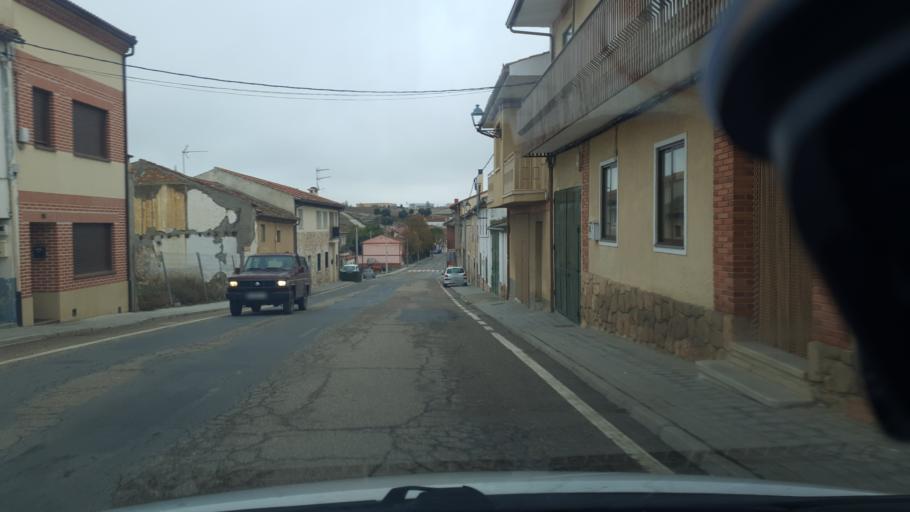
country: ES
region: Castille and Leon
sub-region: Provincia de Segovia
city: Valseca
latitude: 40.9997
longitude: -4.1731
